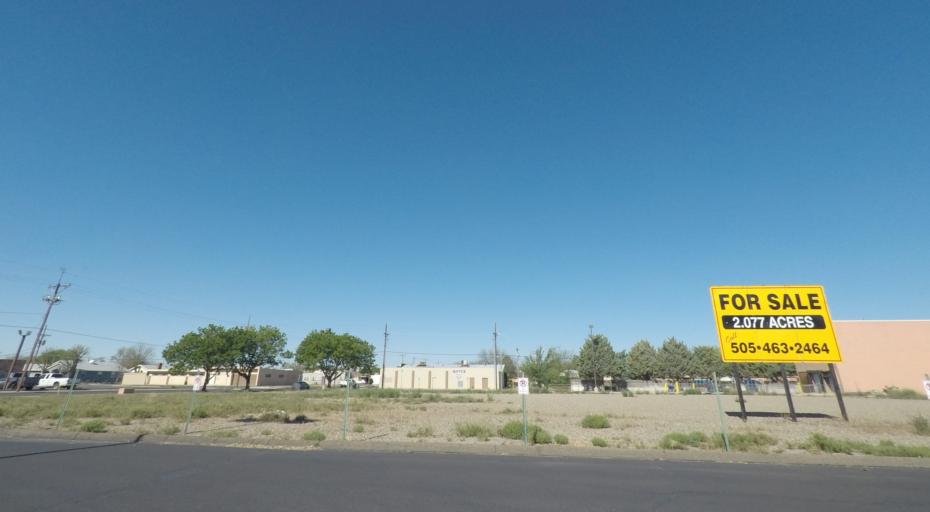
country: US
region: New Mexico
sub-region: Chaves County
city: Roswell
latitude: 33.3801
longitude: -104.5236
